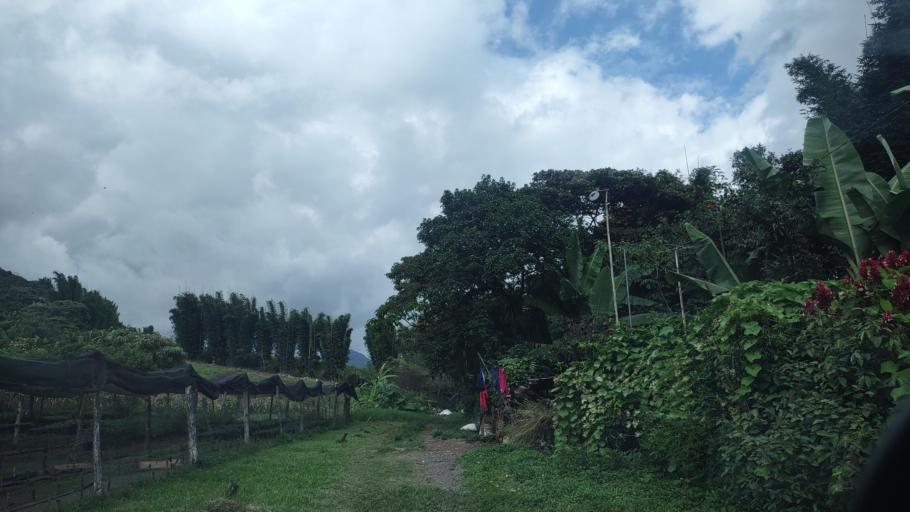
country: MX
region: Veracruz
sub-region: Fortin
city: Monte Salas
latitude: 18.9278
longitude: -97.0273
